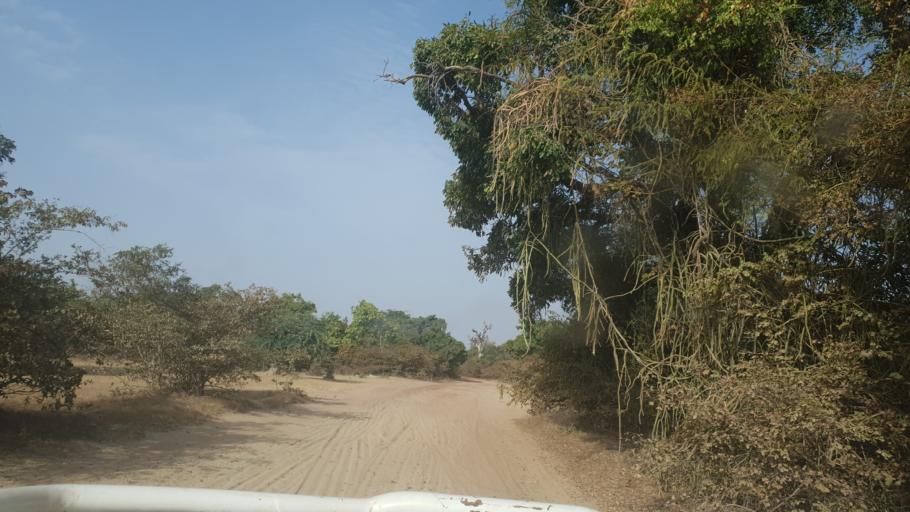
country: ML
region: Segou
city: Baroueli
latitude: 13.3665
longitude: -6.9181
